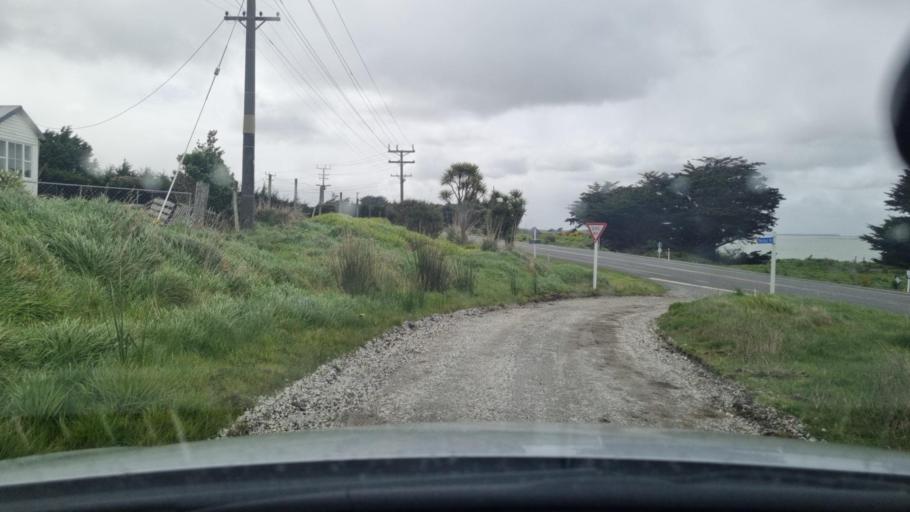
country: NZ
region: Southland
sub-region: Invercargill City
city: Bluff
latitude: -46.5844
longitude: 168.3047
